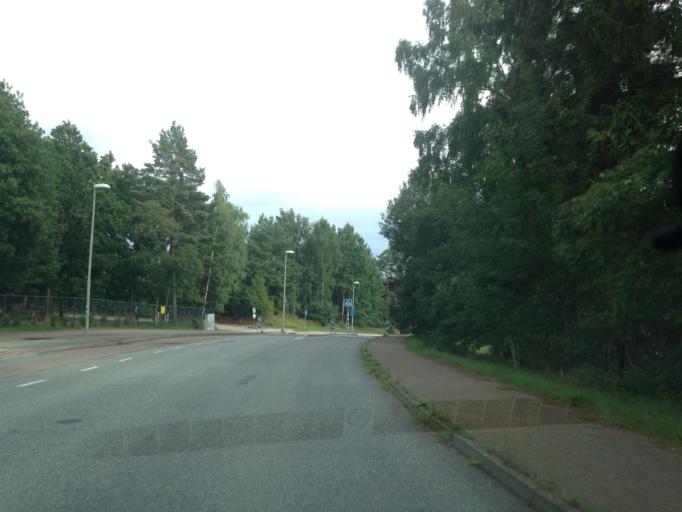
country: SE
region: Vaestra Goetaland
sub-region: Goteborg
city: Goeteborg
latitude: 57.7580
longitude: 11.9672
